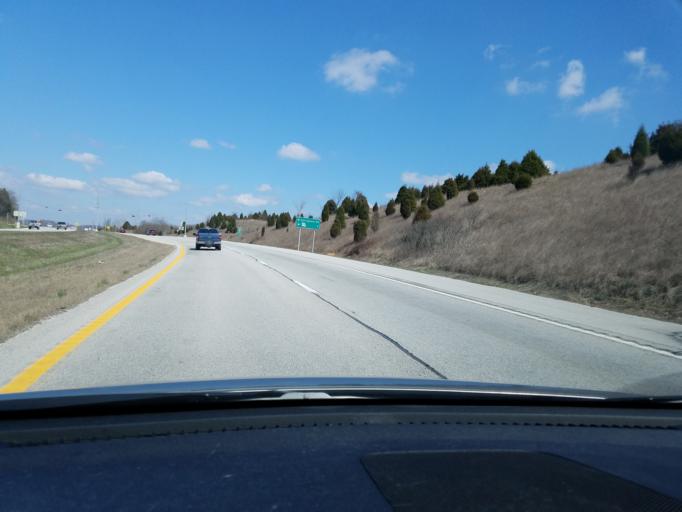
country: US
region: Missouri
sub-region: Taney County
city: Merriam Woods
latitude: 36.8428
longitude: -93.2188
